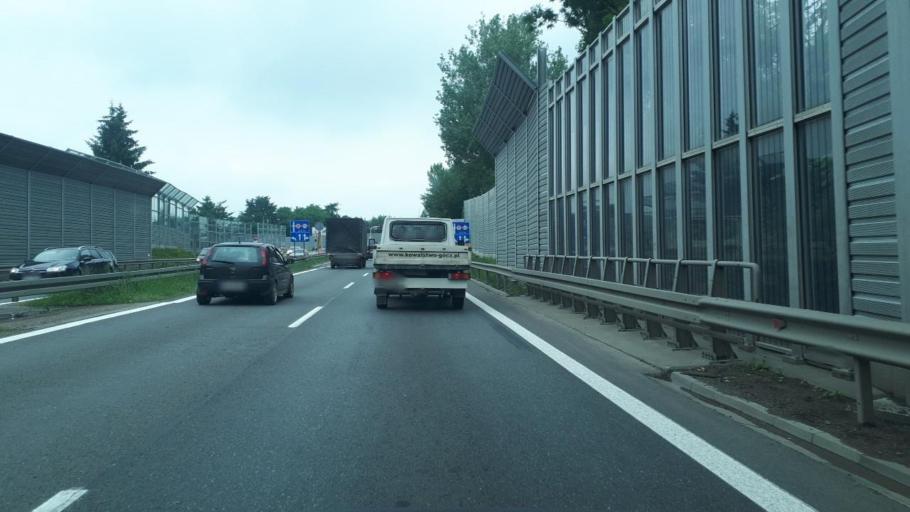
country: PL
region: Silesian Voivodeship
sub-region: Powiat bielski
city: Czechowice-Dziedzice
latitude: 49.9167
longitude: 18.9889
